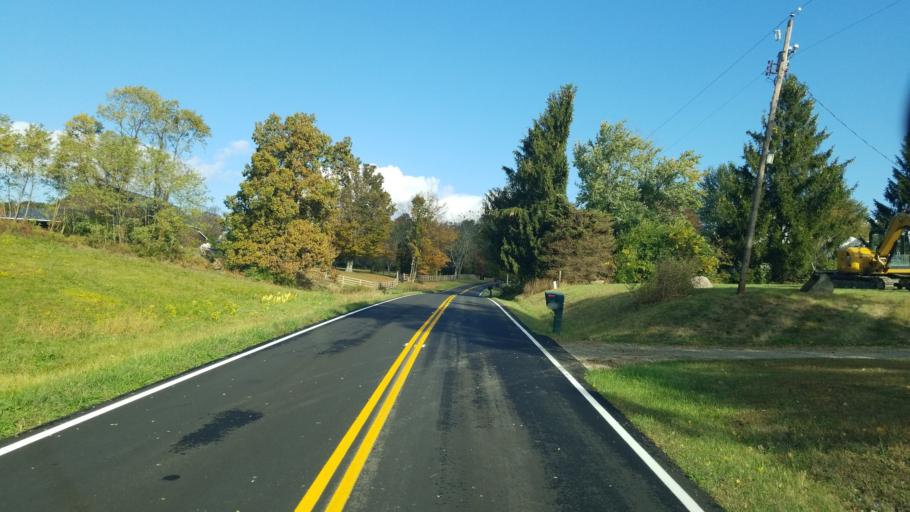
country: US
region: Ohio
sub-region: Warren County
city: Morrow
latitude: 39.4041
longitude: -84.0746
